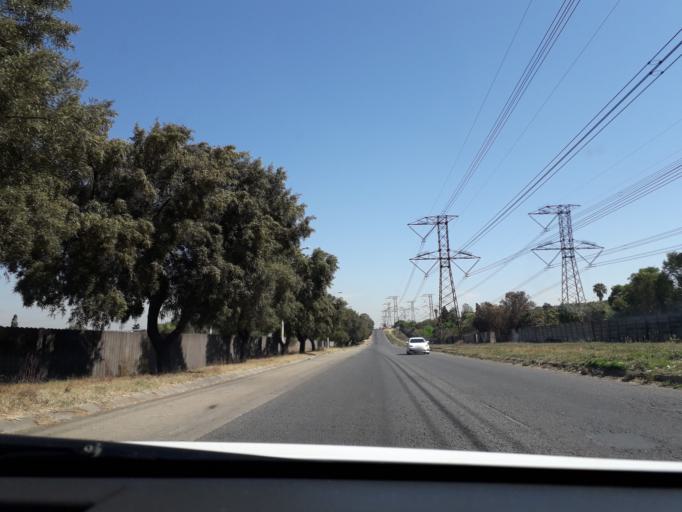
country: ZA
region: Gauteng
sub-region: City of Johannesburg Metropolitan Municipality
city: Modderfontein
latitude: -26.1313
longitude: 28.1906
